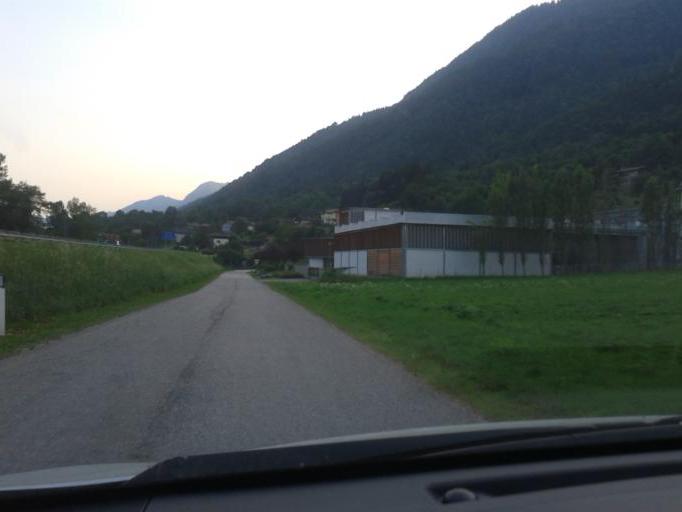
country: IT
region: Trentino-Alto Adige
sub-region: Provincia di Trento
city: Storo
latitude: 45.8589
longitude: 10.5686
